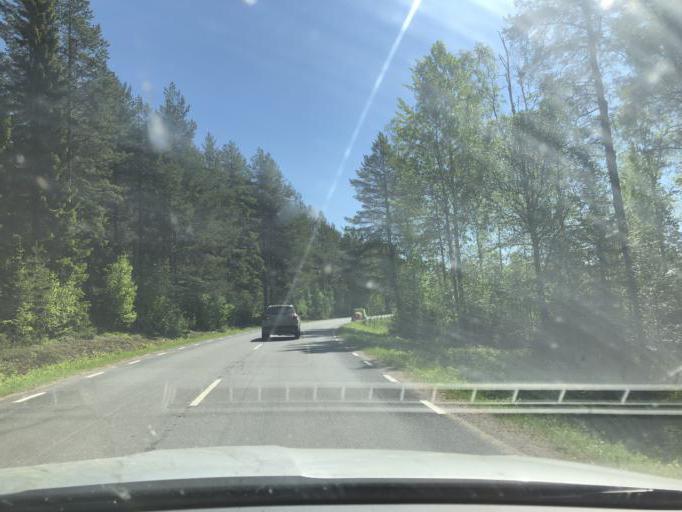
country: SE
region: Norrbotten
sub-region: Lulea Kommun
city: Gammelstad
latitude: 65.6555
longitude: 22.0116
